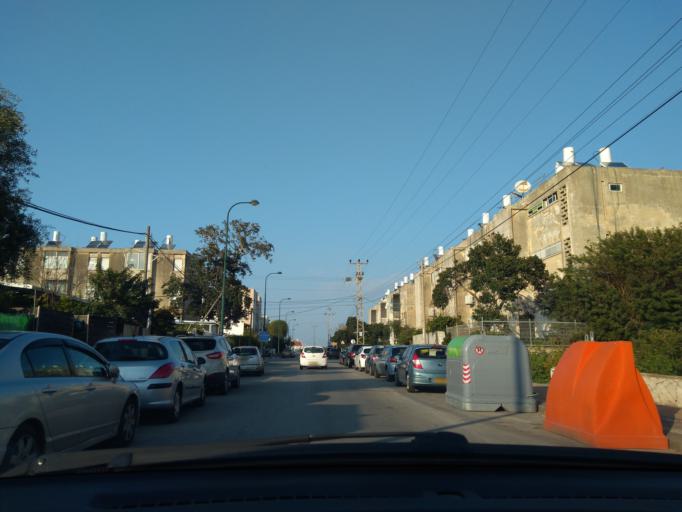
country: IL
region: Central District
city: Even Yehuda
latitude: 32.2804
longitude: 34.8558
